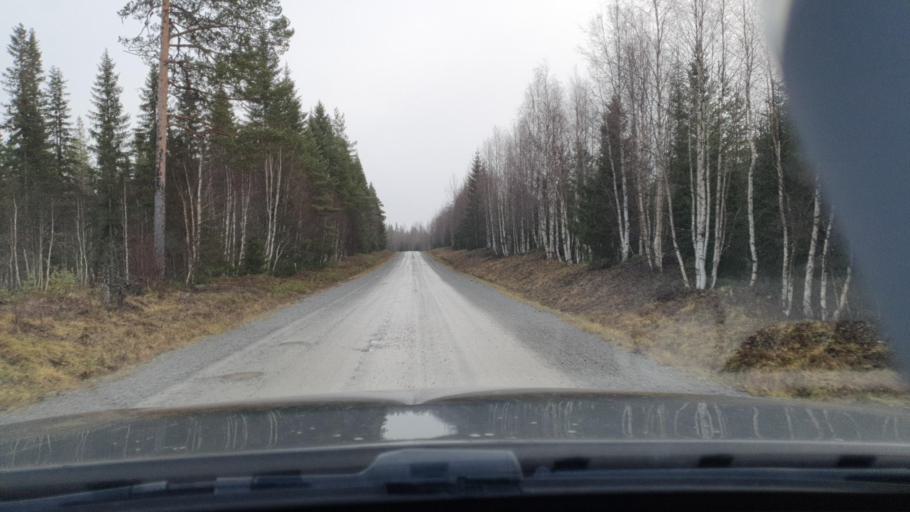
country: SE
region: Jaemtland
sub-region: Stroemsunds Kommun
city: Stroemsund
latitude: 63.5459
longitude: 15.5601
